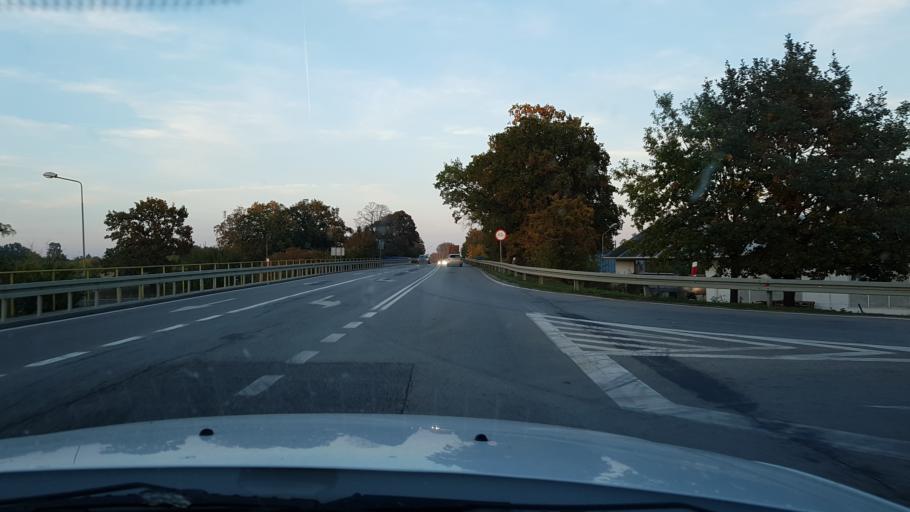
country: PL
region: West Pomeranian Voivodeship
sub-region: Powiat policki
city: Kolbaskowo
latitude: 53.3395
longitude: 14.4422
